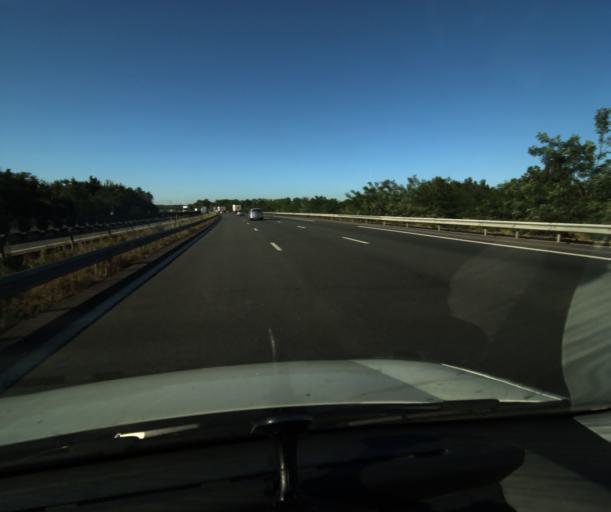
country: FR
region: Midi-Pyrenees
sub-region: Departement du Tarn-et-Garonne
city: Campsas
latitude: 43.9046
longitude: 1.3170
